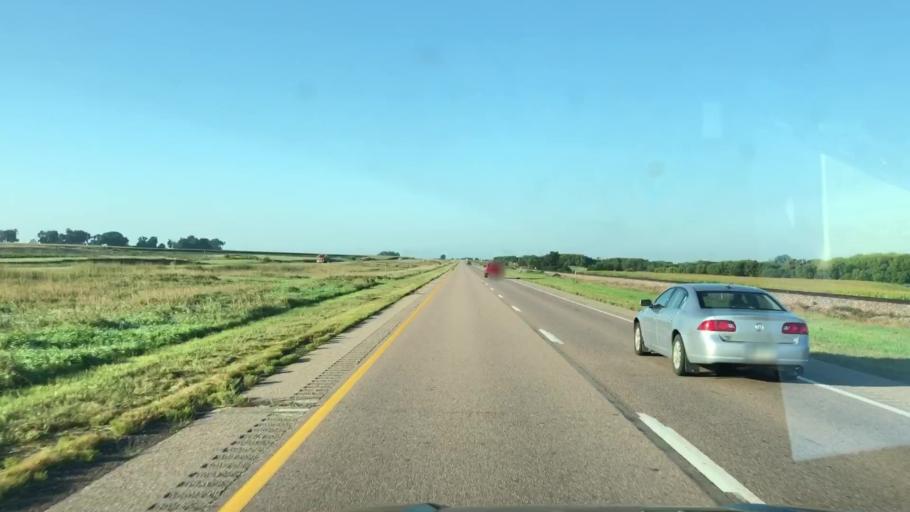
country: US
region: Iowa
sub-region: O'Brien County
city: Sheldon
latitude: 43.1224
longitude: -95.8888
